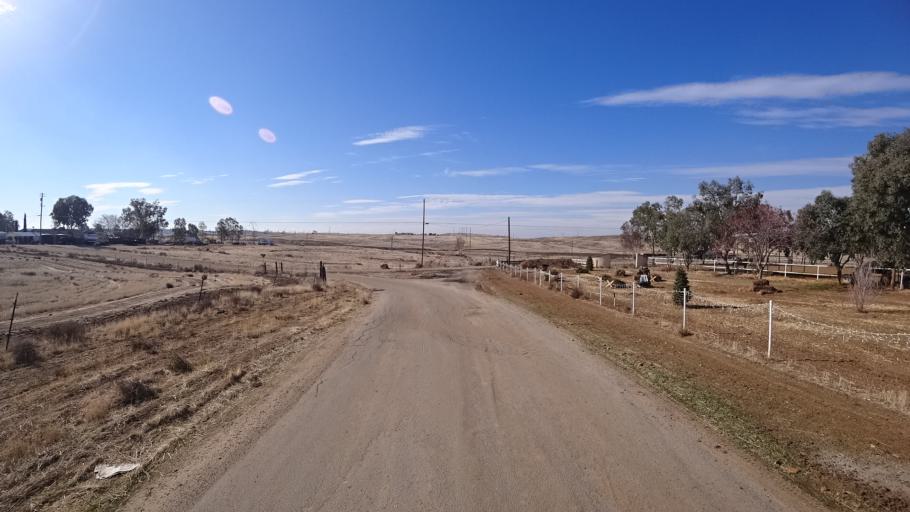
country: US
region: California
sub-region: Kern County
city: Oildale
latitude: 35.4161
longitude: -118.8981
